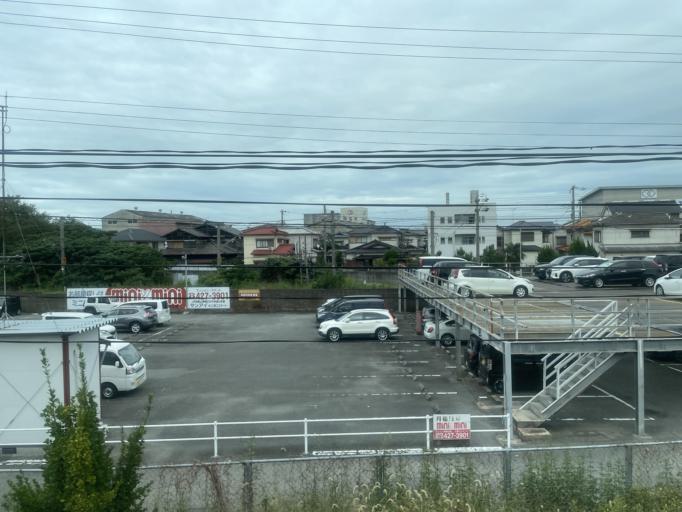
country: JP
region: Wakayama
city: Wakayama-shi
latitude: 34.2391
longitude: 135.1897
